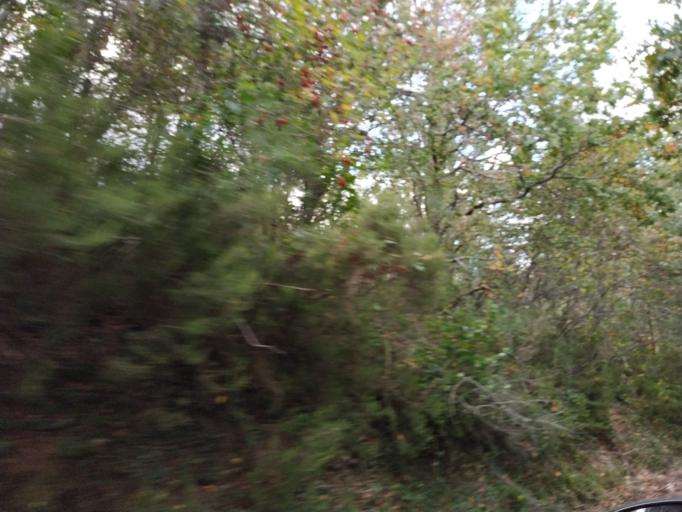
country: ES
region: Castille and Leon
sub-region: Provincia de Leon
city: Candin
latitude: 42.8633
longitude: -6.8636
